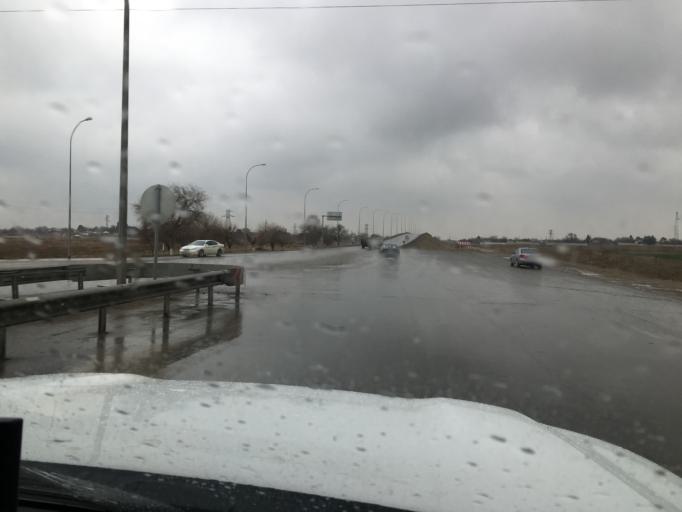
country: TM
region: Mary
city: Mary
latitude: 37.5458
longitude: 61.8705
